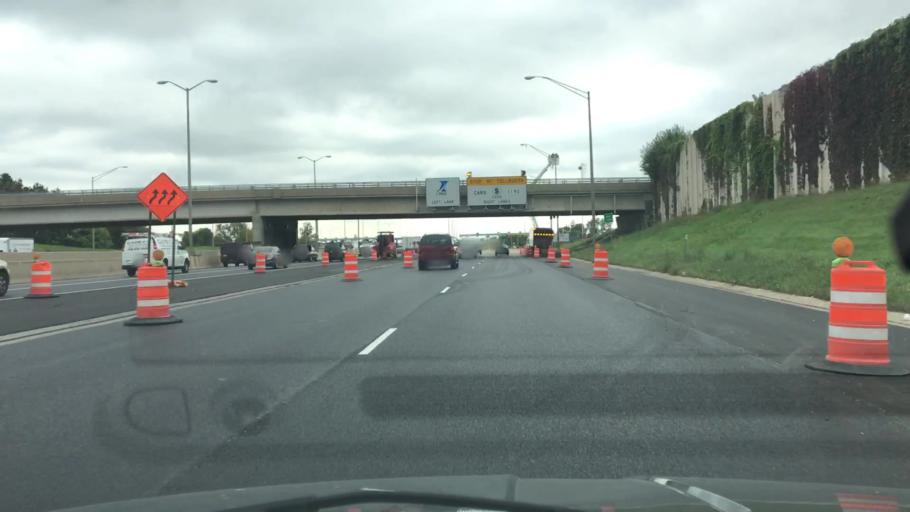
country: US
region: Illinois
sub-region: DuPage County
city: Woodridge
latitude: 41.7370
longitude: -88.0352
